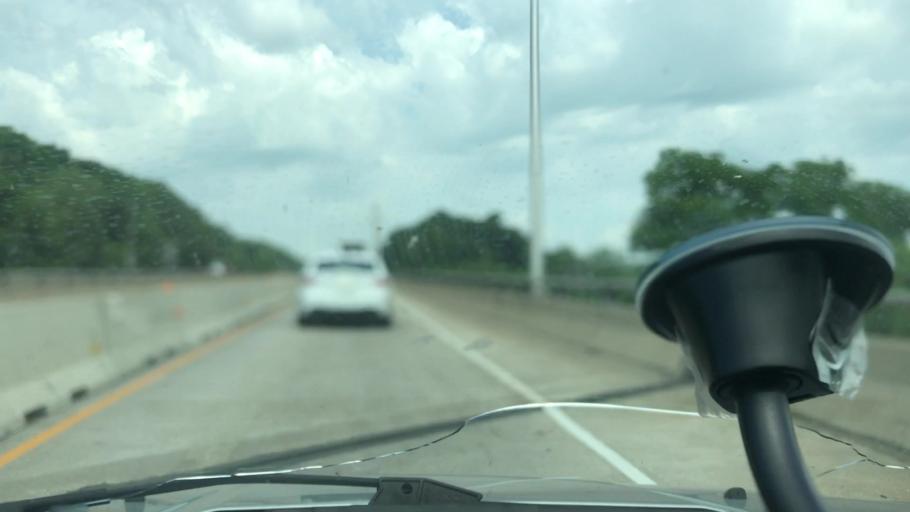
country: US
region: Illinois
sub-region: Peoria County
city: Bartonville
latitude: 40.6612
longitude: -89.6493
